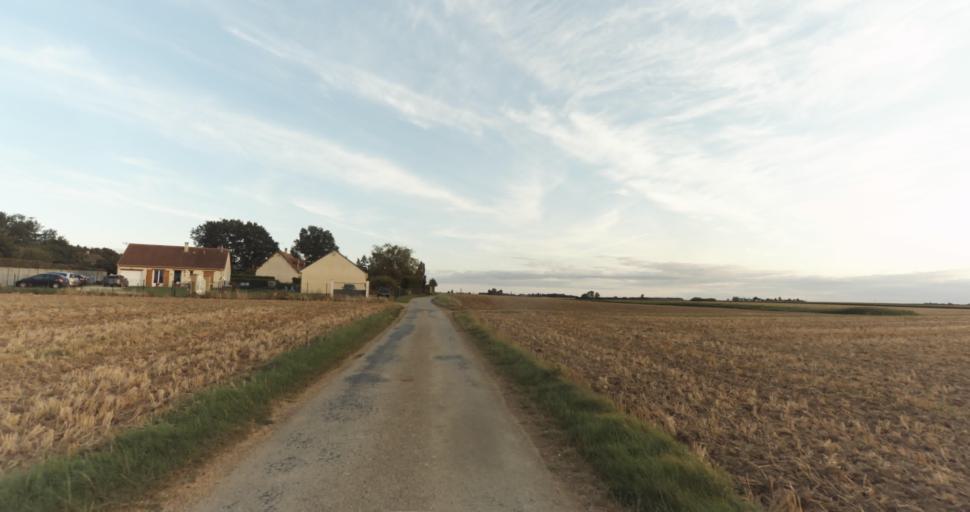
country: FR
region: Haute-Normandie
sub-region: Departement de l'Eure
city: La Madeleine-de-Nonancourt
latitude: 48.8952
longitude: 1.2352
